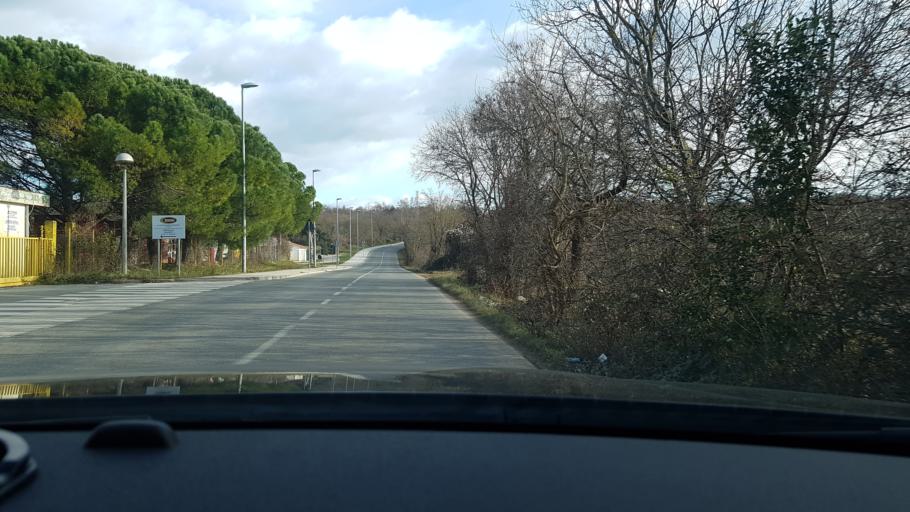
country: HR
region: Istarska
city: Vinez
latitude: 45.1074
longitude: 14.1101
